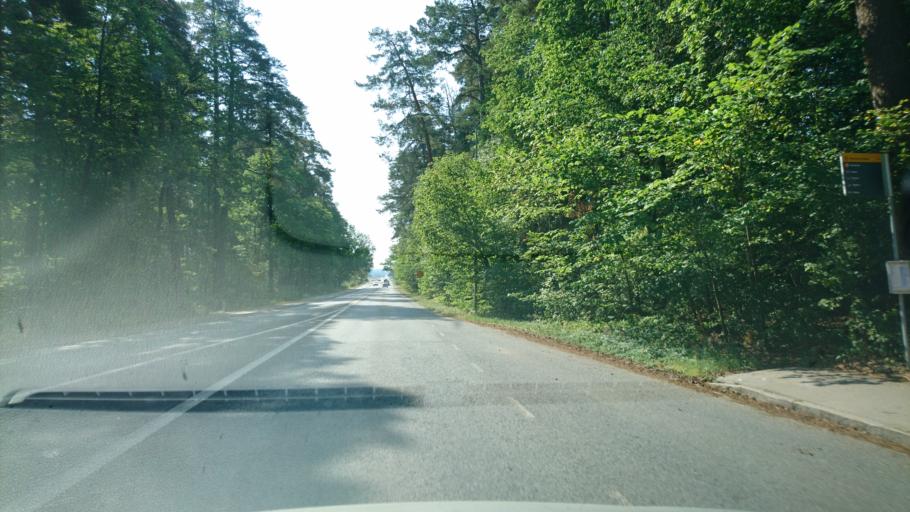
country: SE
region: Uppsala
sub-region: Uppsala Kommun
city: Uppsala
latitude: 59.8276
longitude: 17.6444
